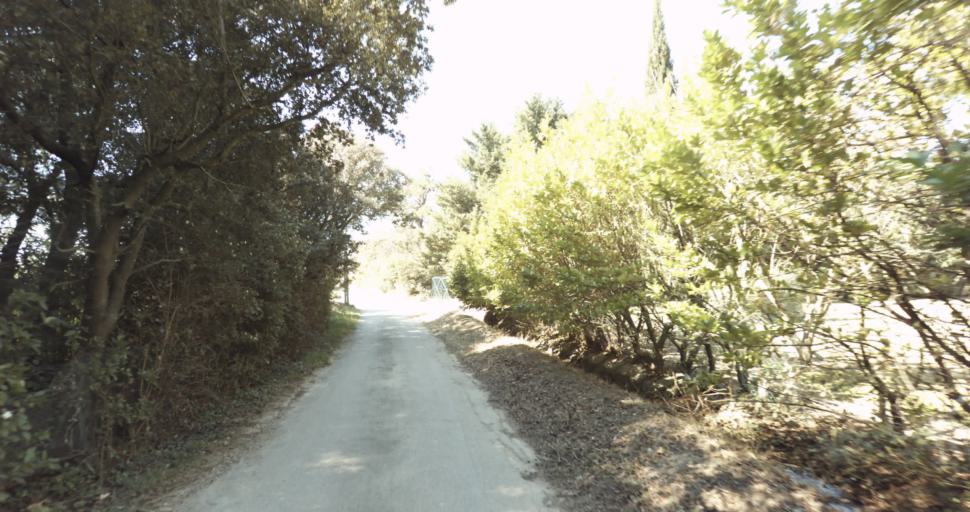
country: FR
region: Provence-Alpes-Cote d'Azur
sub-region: Departement des Bouches-du-Rhone
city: Pelissanne
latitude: 43.6242
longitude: 5.1641
